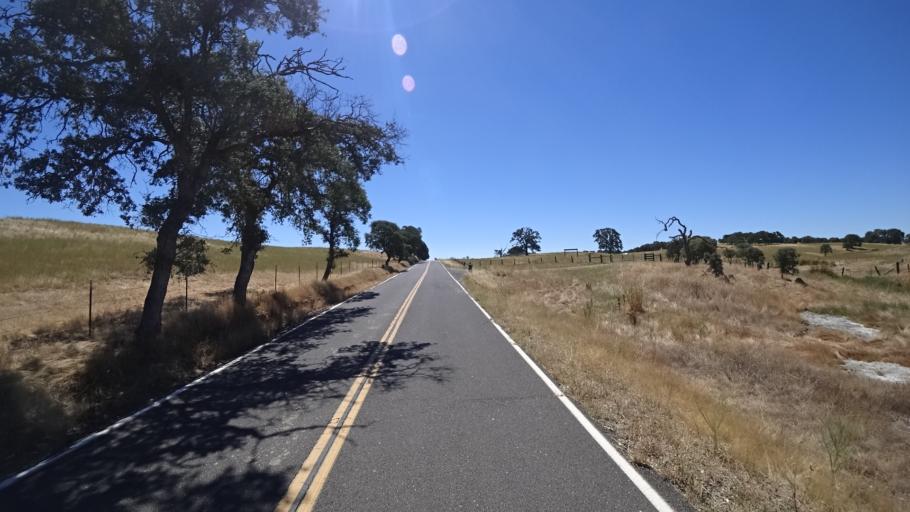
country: US
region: California
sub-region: Calaveras County
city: Copperopolis
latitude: 38.0251
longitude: -120.7192
